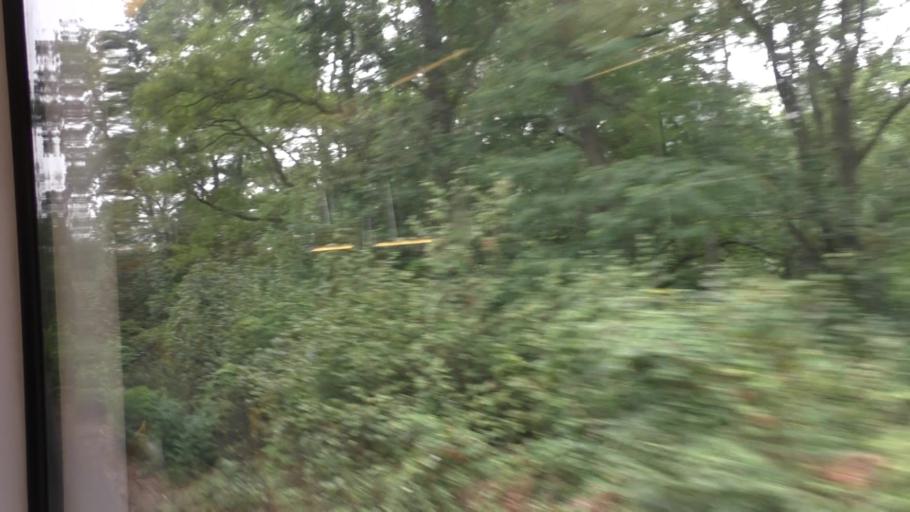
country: DE
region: Saxony
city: Zittau
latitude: 50.9085
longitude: 14.8206
